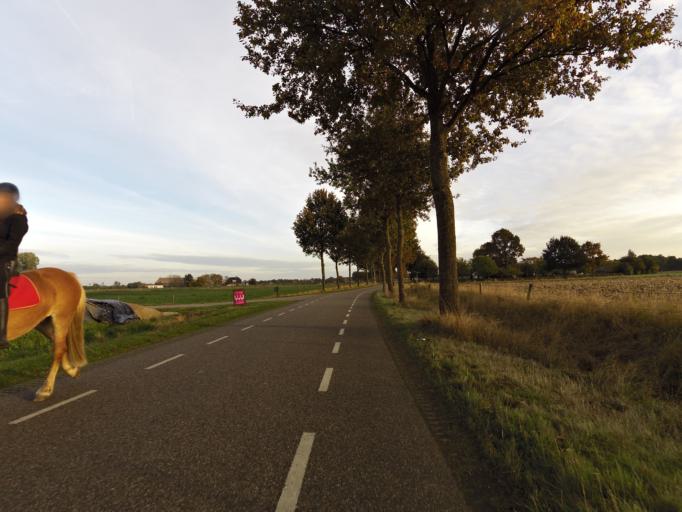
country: NL
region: Gelderland
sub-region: Gemeente Doesburg
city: Doesburg
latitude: 51.9727
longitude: 6.1883
